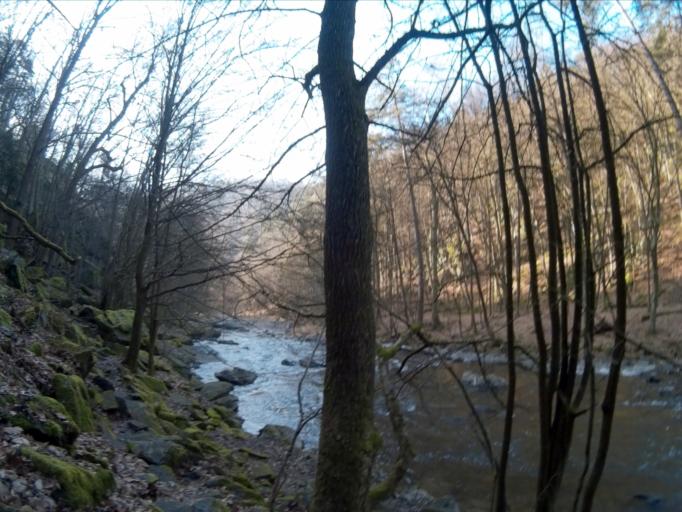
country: CZ
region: Vysocina
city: Namest' nad Oslavou
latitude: 49.1724
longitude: 16.1647
